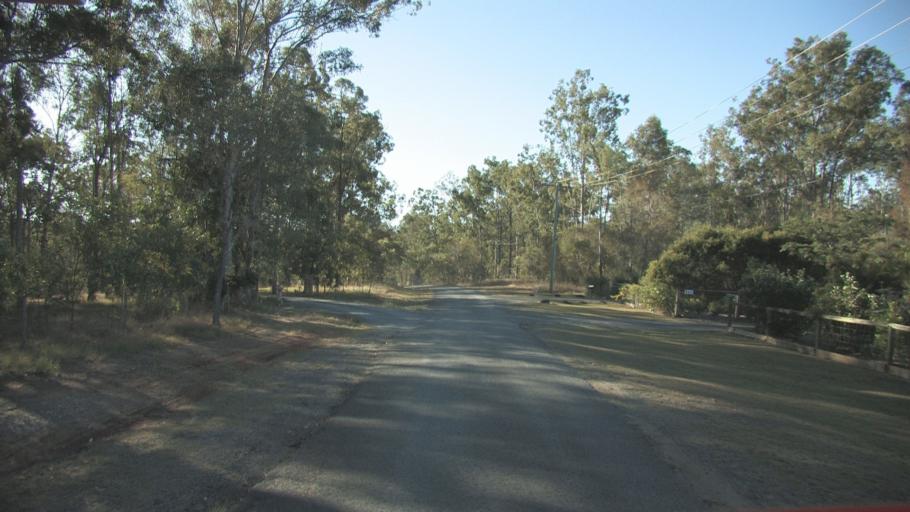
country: AU
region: Queensland
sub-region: Logan
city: North Maclean
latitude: -27.8100
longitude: 153.0496
